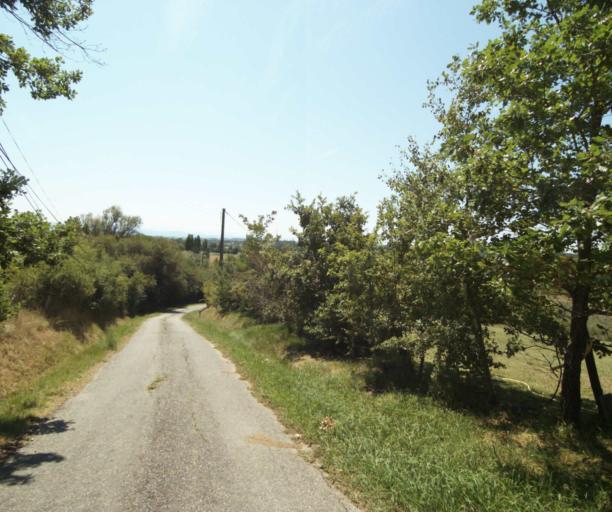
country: FR
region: Midi-Pyrenees
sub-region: Departement de l'Ariege
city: Lezat-sur-Leze
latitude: 43.3064
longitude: 1.3441
